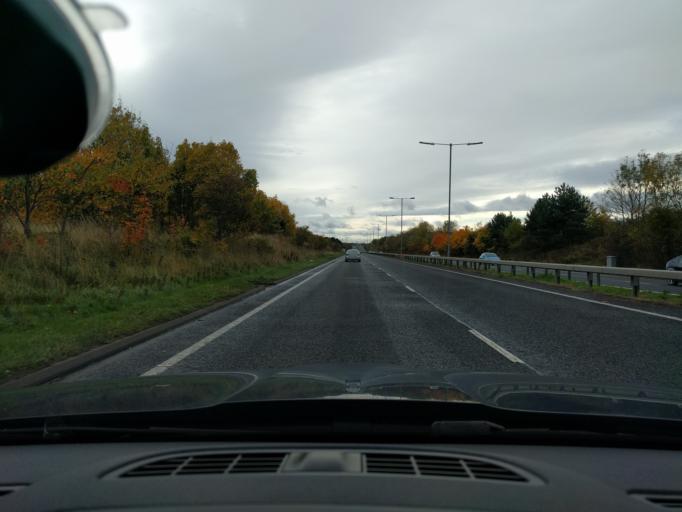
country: GB
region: England
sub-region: Northumberland
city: Newbiggin-by-the-Sea
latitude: 55.1665
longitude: -1.5352
